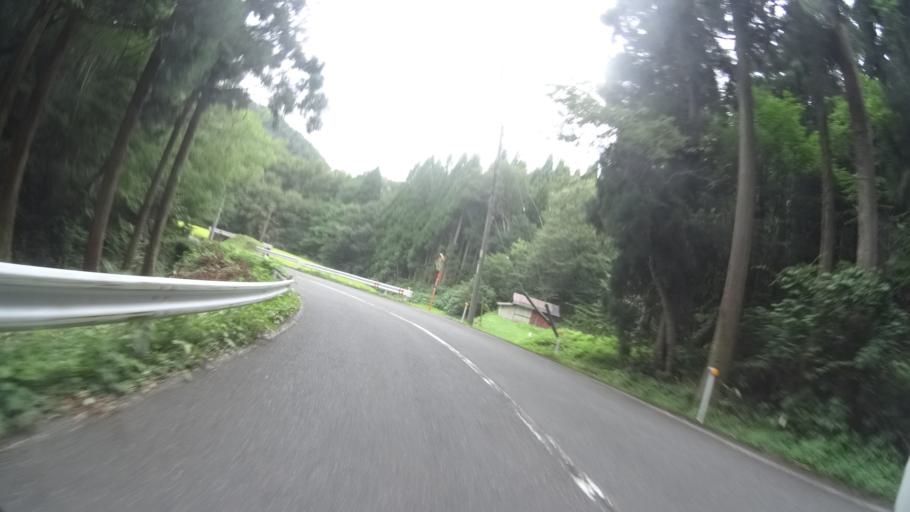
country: JP
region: Tottori
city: Kurayoshi
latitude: 35.4068
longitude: 133.9873
